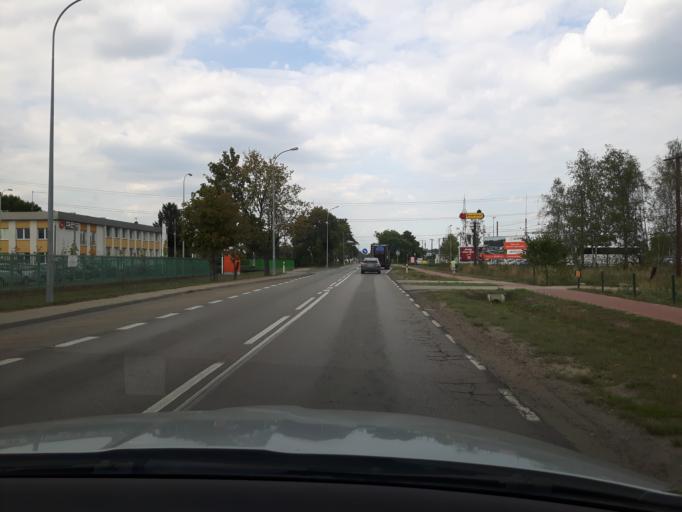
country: PL
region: Masovian Voivodeship
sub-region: Powiat legionowski
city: Stanislawow Pierwszy
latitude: 52.3691
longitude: 21.0288
